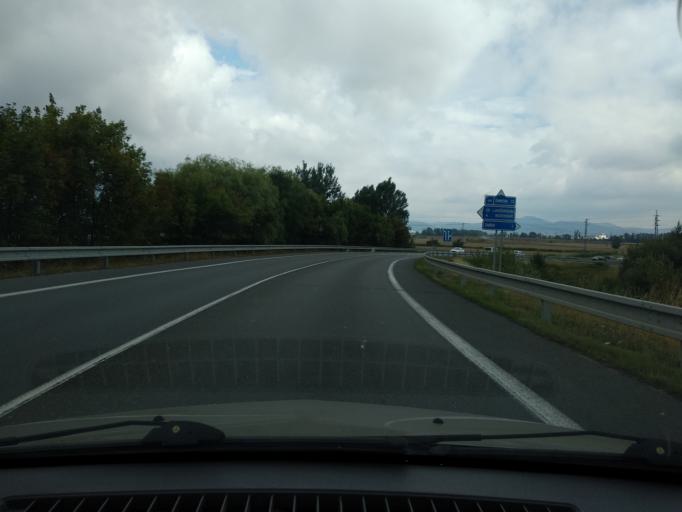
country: CZ
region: Olomoucky
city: Zabreh
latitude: 49.8882
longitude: 16.8921
